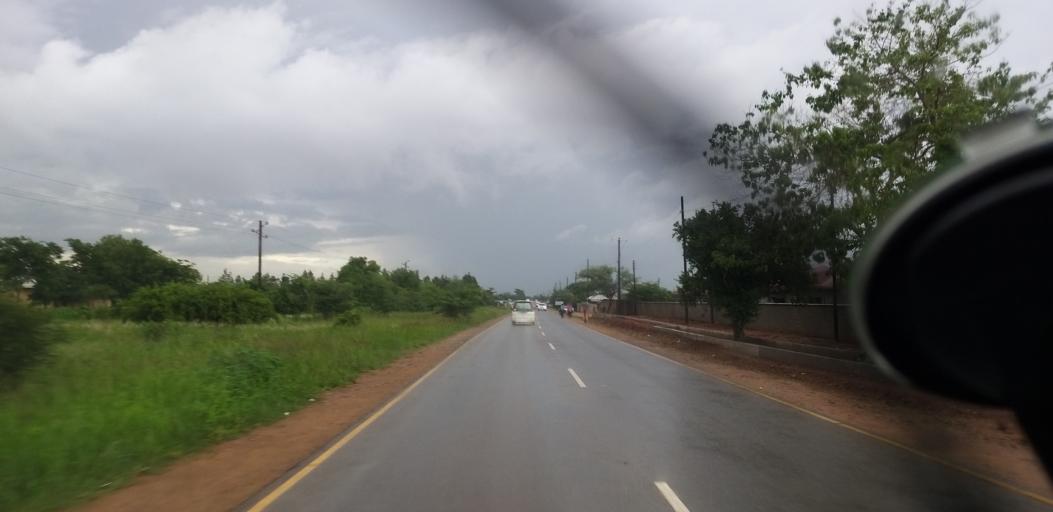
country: ZM
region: Lusaka
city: Lusaka
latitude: -15.4799
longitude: 28.3157
